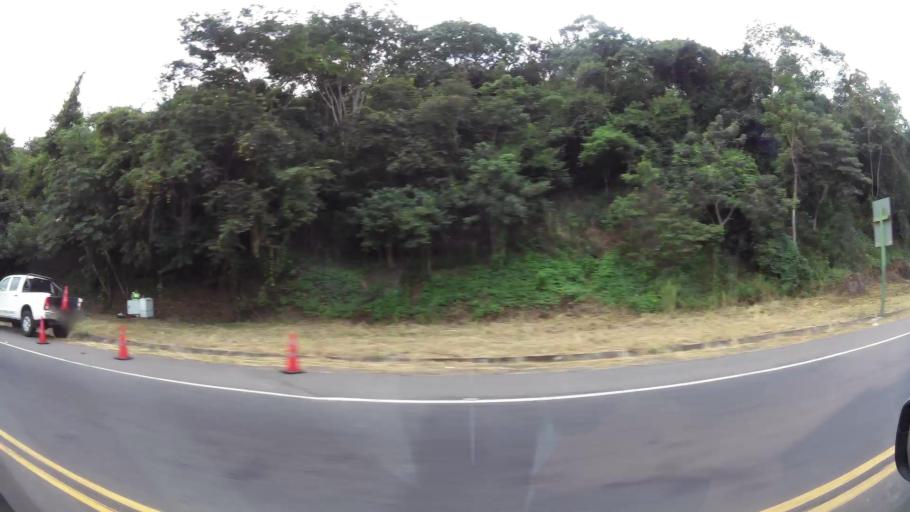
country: CR
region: Puntarenas
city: Esparza
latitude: 9.9183
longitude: -84.7048
